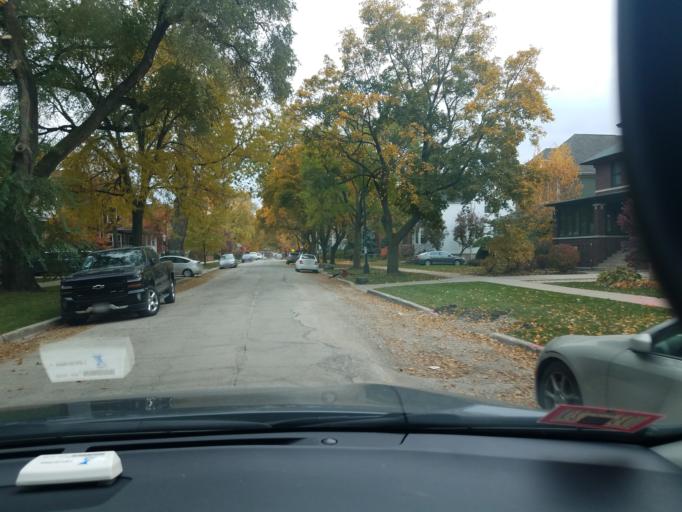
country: US
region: Illinois
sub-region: Cook County
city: Lincolnwood
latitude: 41.9602
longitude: -87.7327
